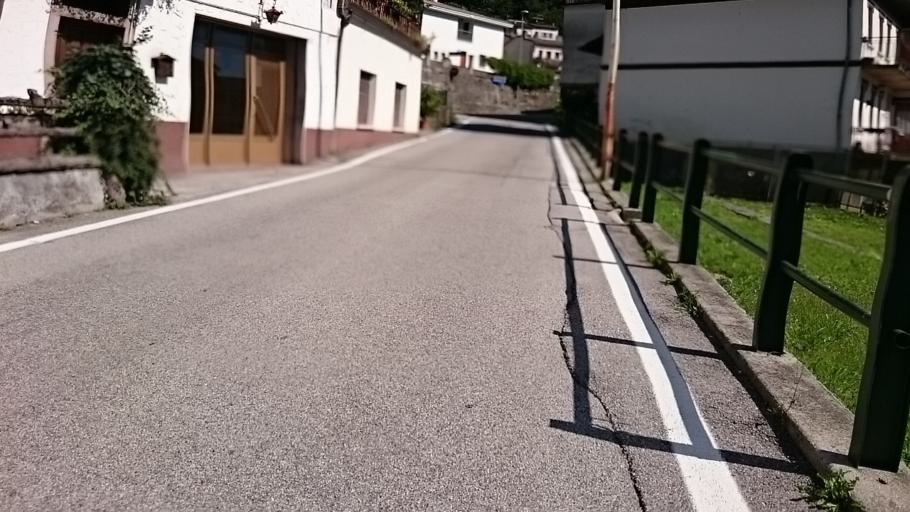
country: IT
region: Veneto
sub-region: Provincia di Belluno
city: Castello Lavazzo
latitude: 46.2769
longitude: 12.3105
